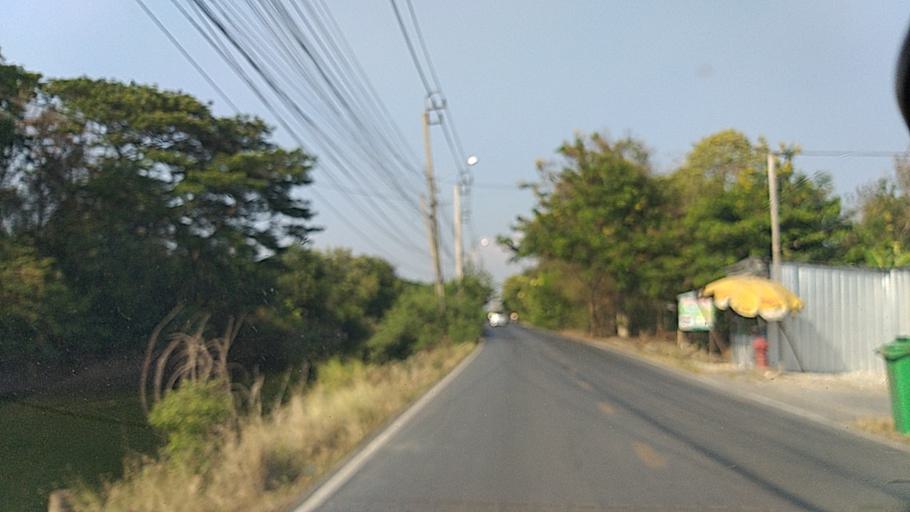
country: TH
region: Nonthaburi
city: Sai Noi
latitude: 13.9390
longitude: 100.3480
